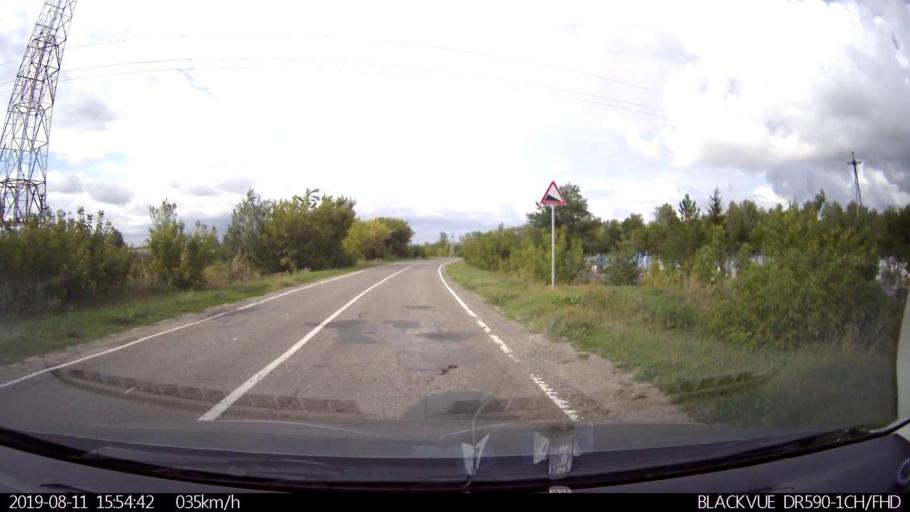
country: RU
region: Ulyanovsk
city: Ignatovka
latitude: 53.9425
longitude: 47.6561
